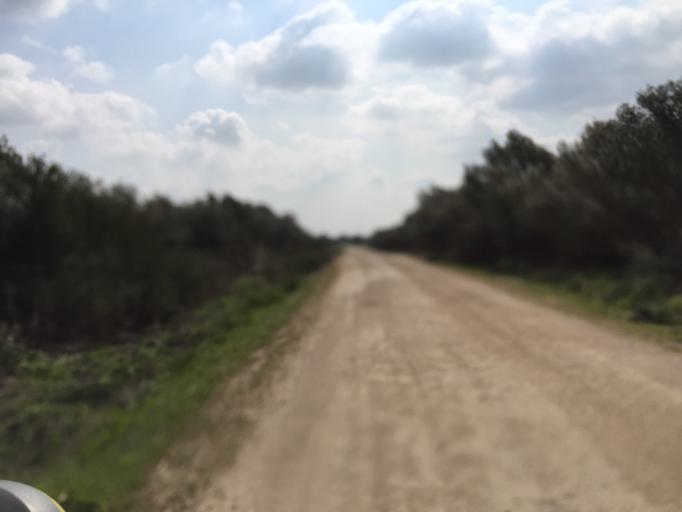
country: ES
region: Andalusia
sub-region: Provincia de Cadiz
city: Benalup-Casas Viejas
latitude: 36.3278
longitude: -5.8891
